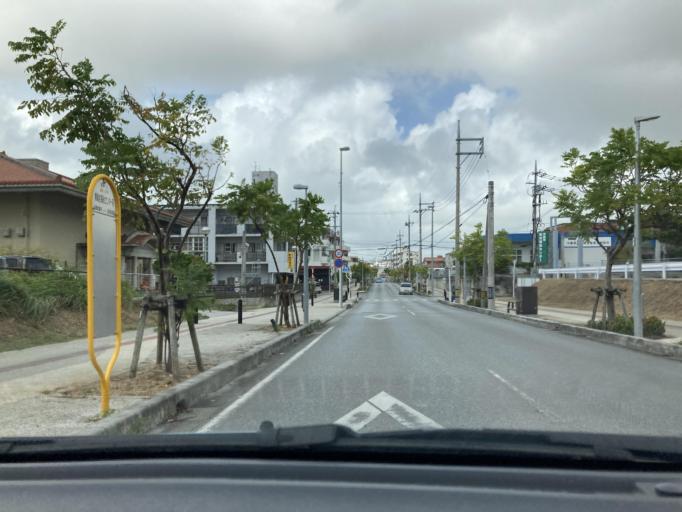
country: JP
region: Okinawa
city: Ginowan
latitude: 26.2310
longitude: 127.7332
